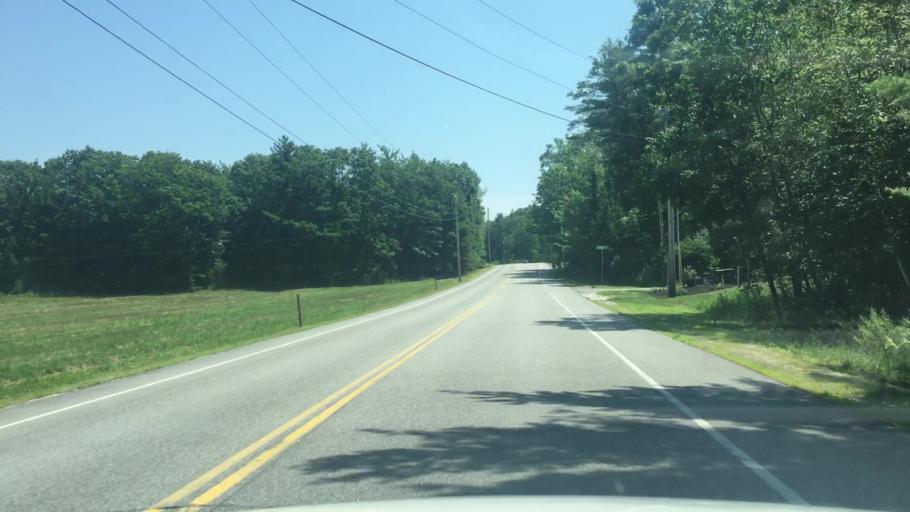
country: US
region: Maine
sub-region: Cumberland County
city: Falmouth
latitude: 43.7438
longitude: -70.2563
